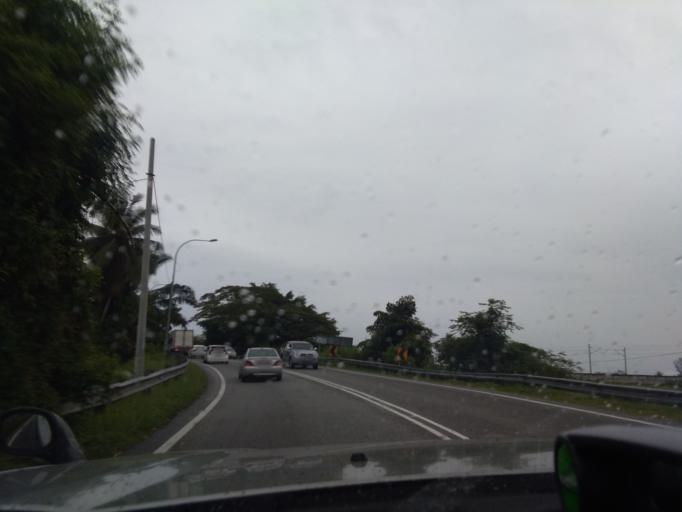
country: MY
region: Penang
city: Nibong Tebal
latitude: 5.1625
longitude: 100.4789
